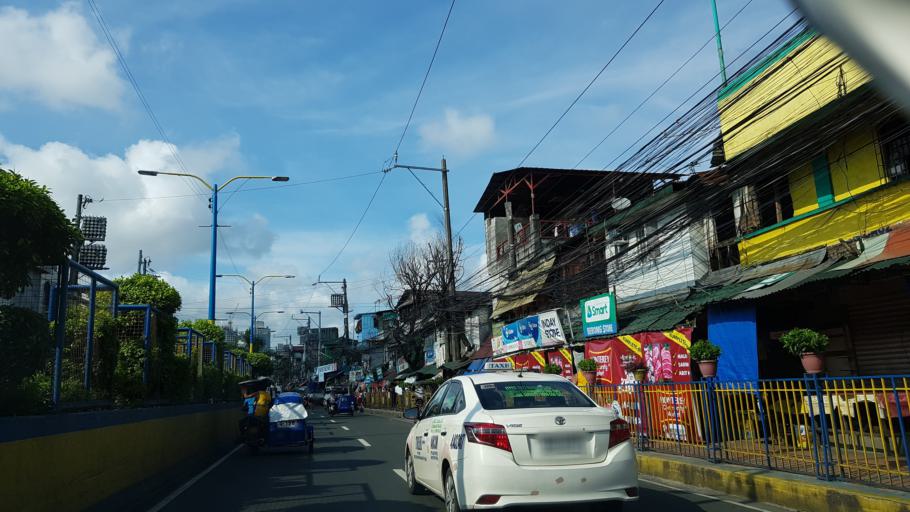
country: PH
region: Metro Manila
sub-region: Mandaluyong
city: Mandaluyong City
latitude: 14.5802
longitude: 121.0363
